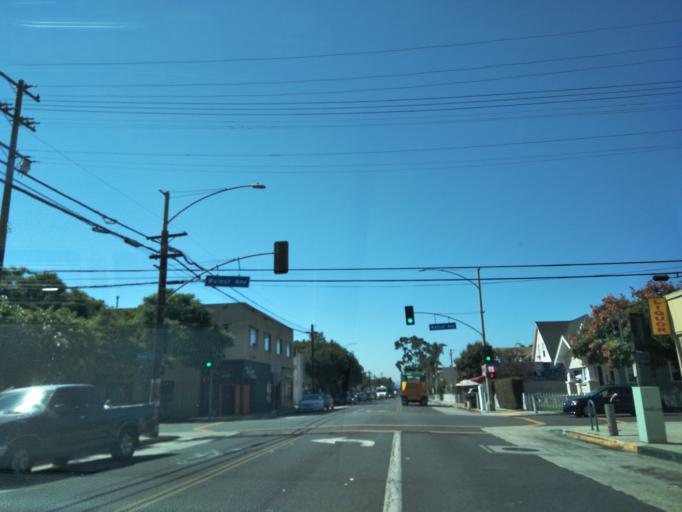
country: US
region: California
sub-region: Los Angeles County
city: Long Beach
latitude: 33.7717
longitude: -118.1718
